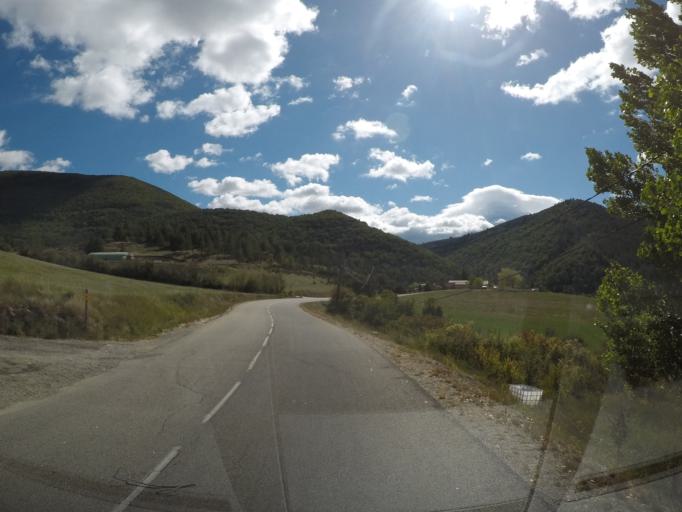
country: FR
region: Provence-Alpes-Cote d'Azur
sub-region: Departement du Vaucluse
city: Sault
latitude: 44.1686
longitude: 5.4326
